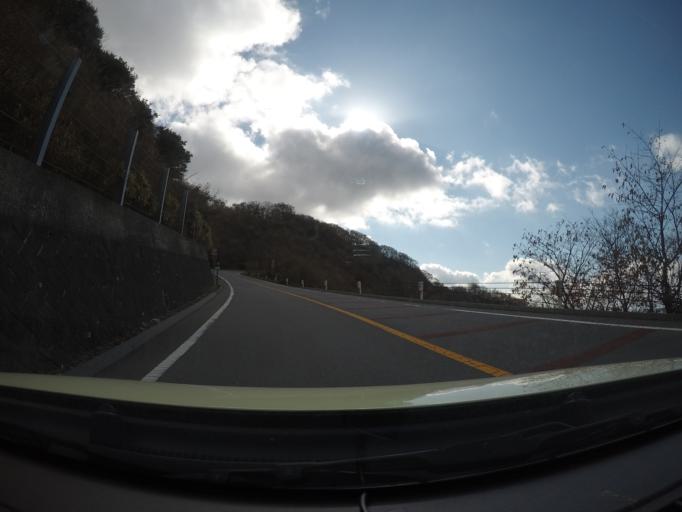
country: JP
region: Shizuoka
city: Gotemba
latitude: 35.2514
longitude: 138.9742
